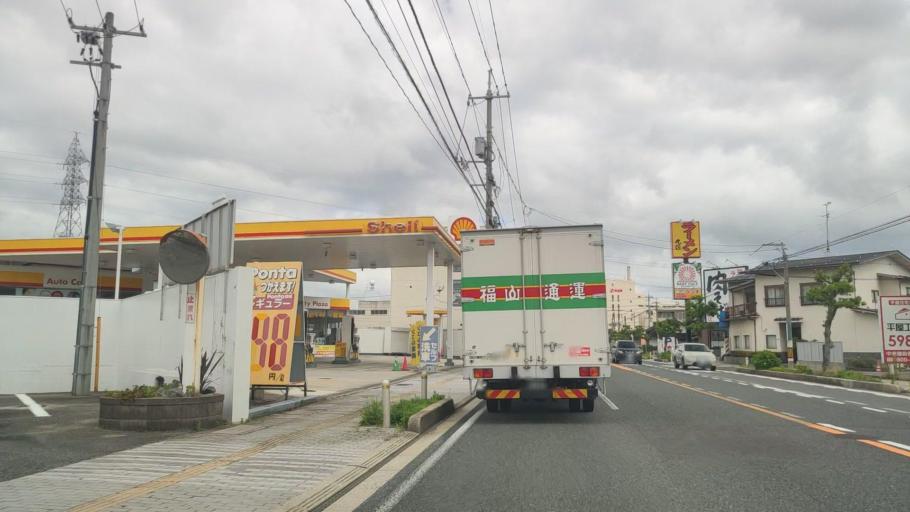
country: JP
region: Tottori
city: Yonago
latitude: 35.4338
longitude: 133.3502
